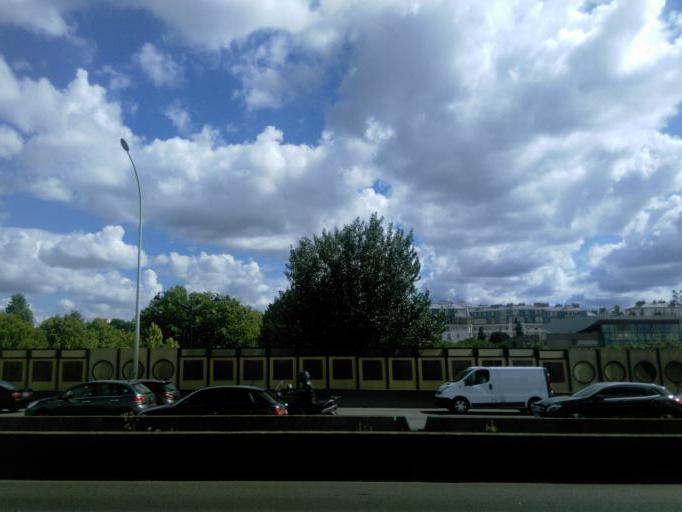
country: FR
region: Ile-de-France
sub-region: Paris
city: Saint-Ouen
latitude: 48.9011
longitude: 2.3436
